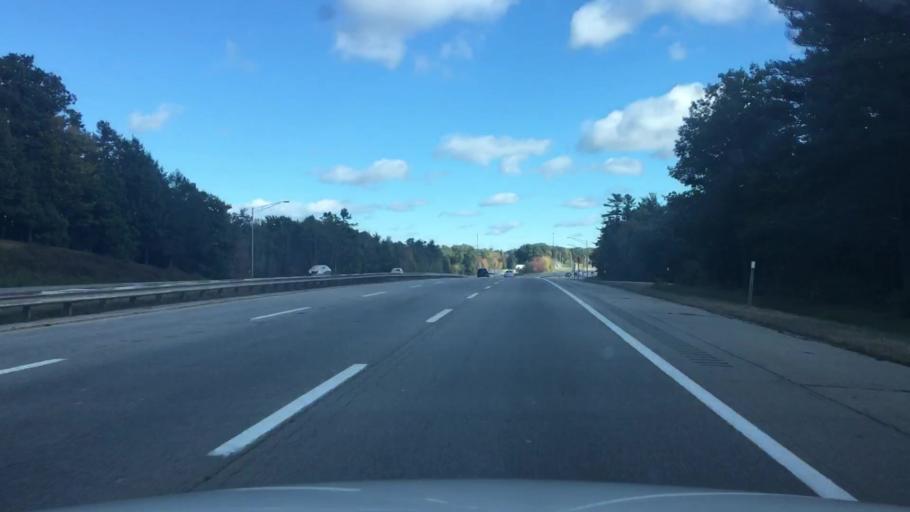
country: US
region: Maine
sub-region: York County
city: Kittery
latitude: 43.1302
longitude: -70.7172
